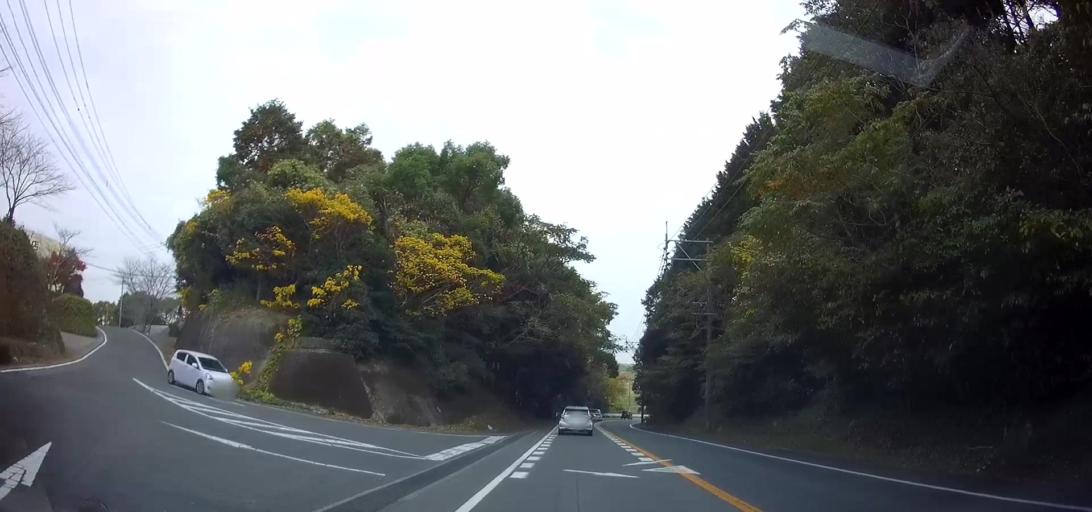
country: JP
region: Nagasaki
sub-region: Isahaya-shi
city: Isahaya
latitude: 32.7881
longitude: 130.0462
